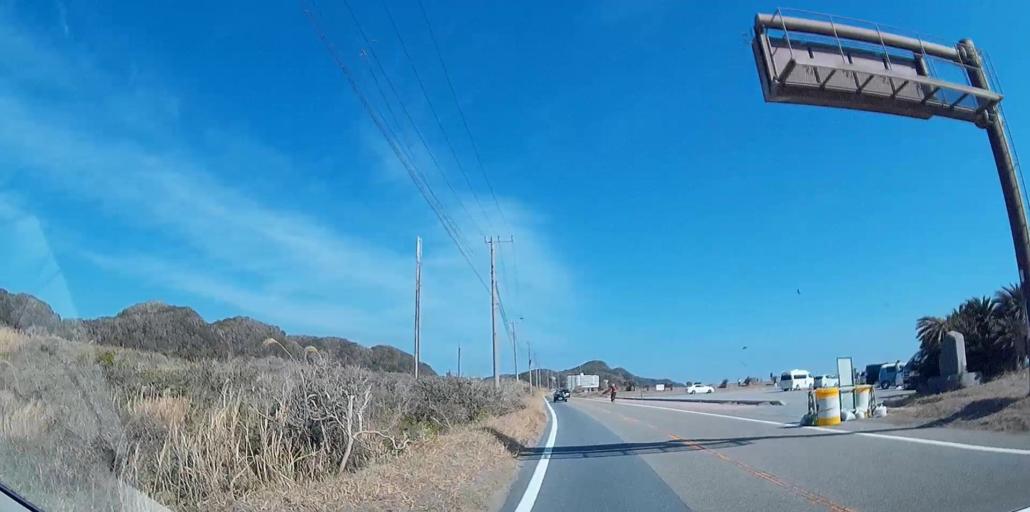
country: JP
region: Chiba
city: Tateyama
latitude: 34.9066
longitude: 139.8588
